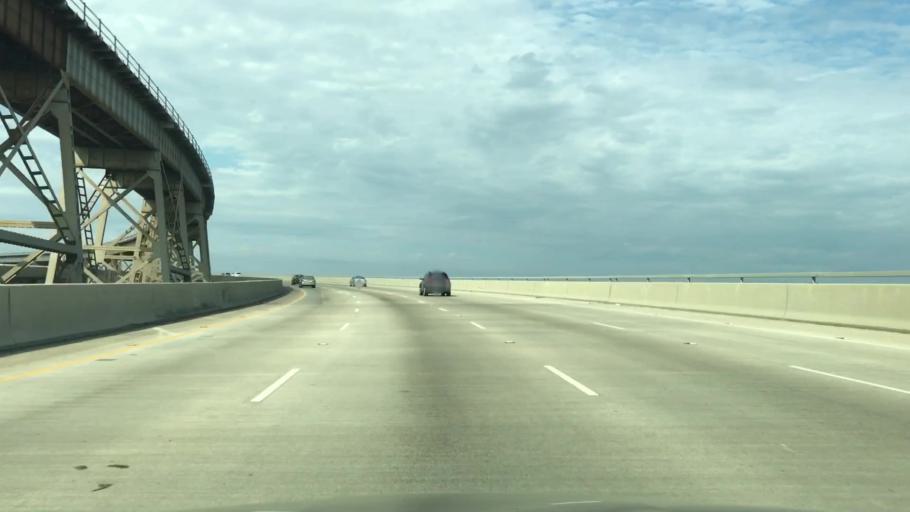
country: US
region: Louisiana
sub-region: Jefferson Parish
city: Bridge City
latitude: 29.9362
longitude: -90.1628
